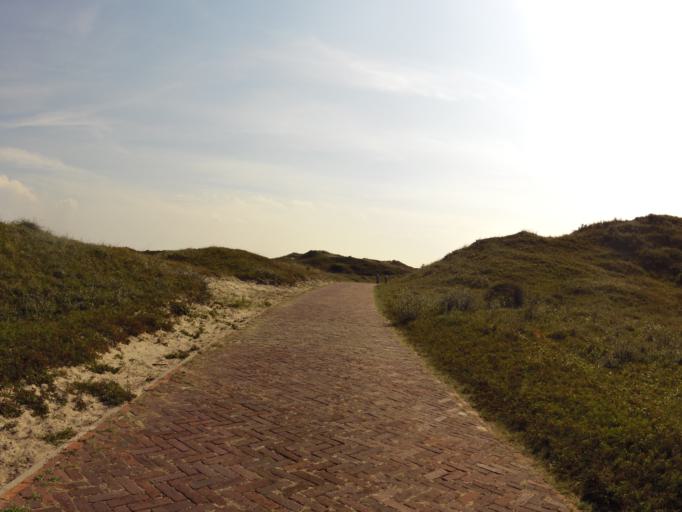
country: NL
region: North Holland
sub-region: Gemeente Bergen
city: Egmond aan Zee
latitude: 52.6542
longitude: 4.6311
